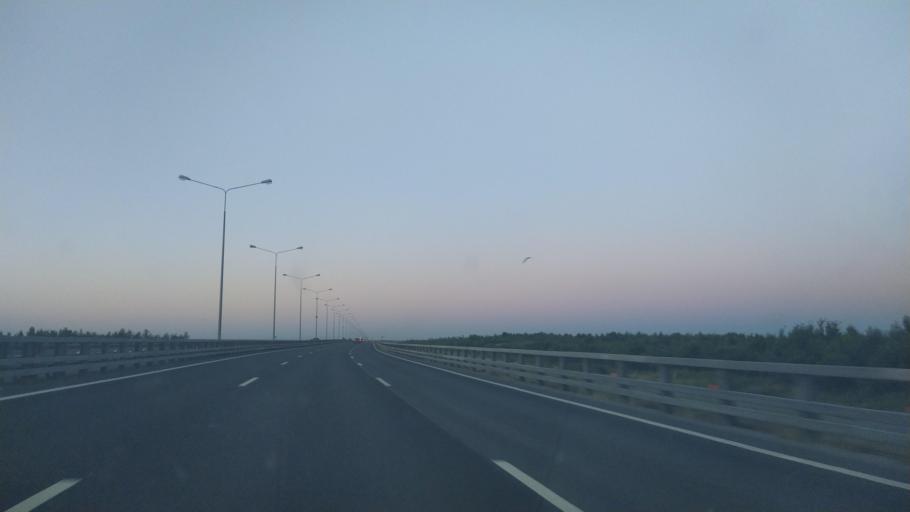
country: RU
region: St.-Petersburg
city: Kronshtadt
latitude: 60.0197
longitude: 29.7398
